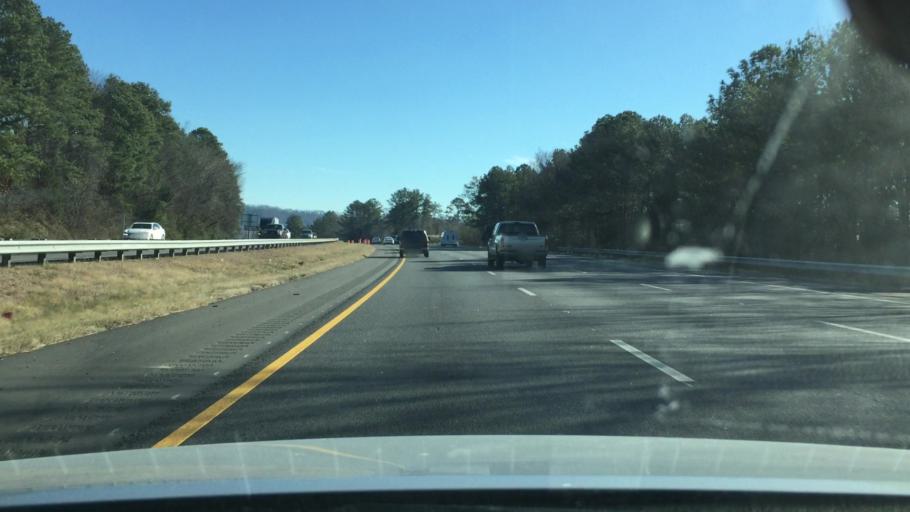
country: US
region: Georgia
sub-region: Catoosa County
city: Ringgold
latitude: 34.9158
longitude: -85.1447
